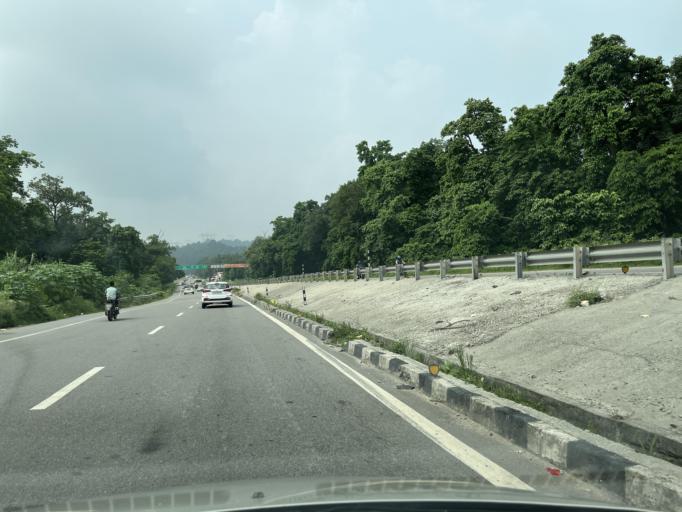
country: IN
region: Uttarakhand
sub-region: Dehradun
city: Raiwala
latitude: 30.0510
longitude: 78.2172
